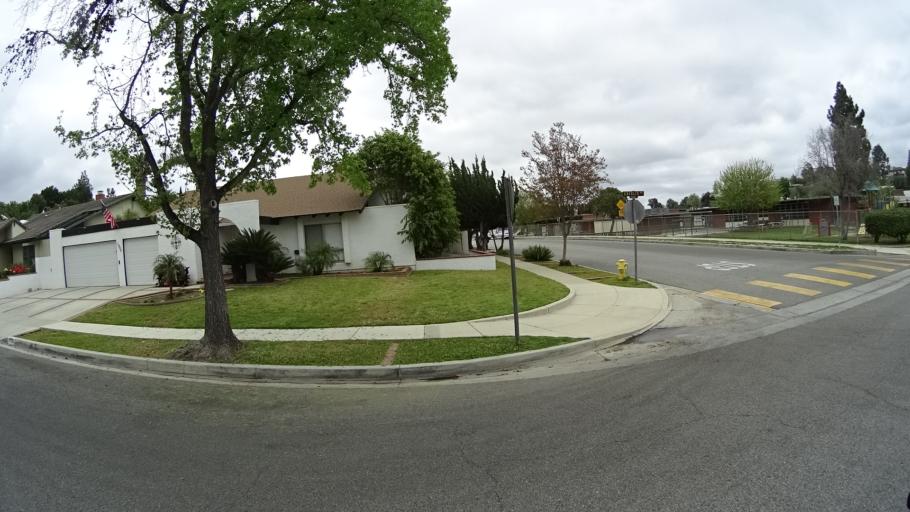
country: US
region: California
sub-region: Ventura County
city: Thousand Oaks
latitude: 34.2037
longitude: -118.8835
